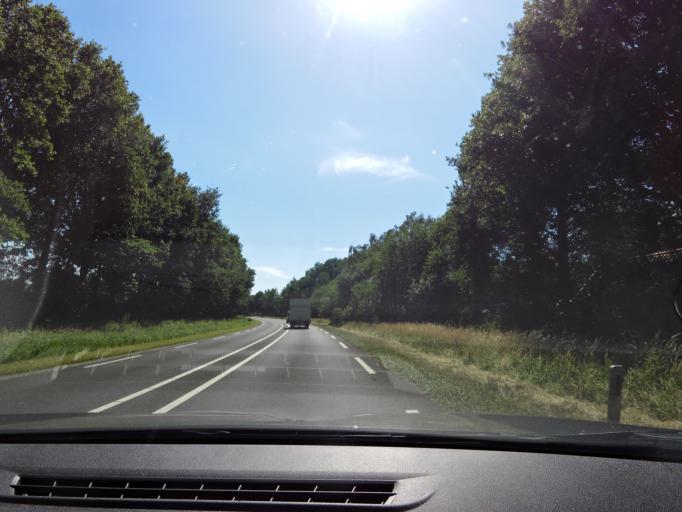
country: NL
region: Gelderland
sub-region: Oost Gelre
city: Lichtenvoorde
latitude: 52.0310
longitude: 6.6158
